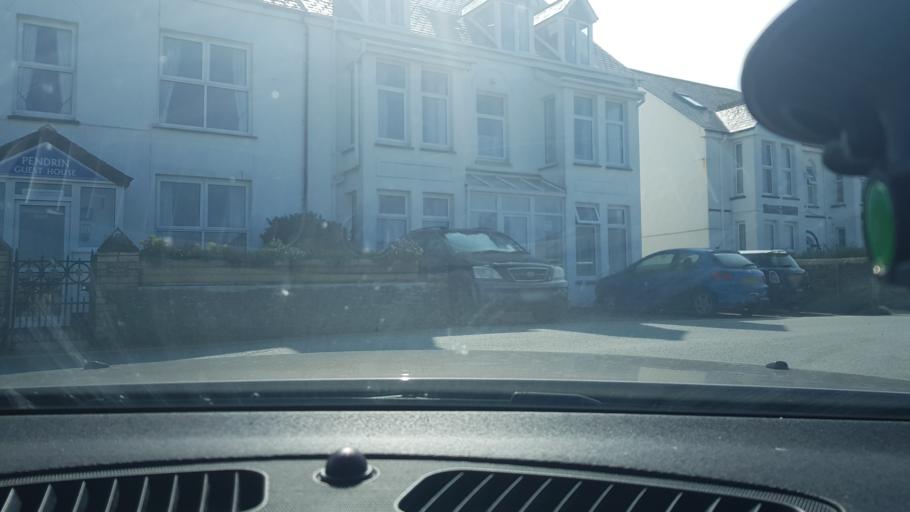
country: GB
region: England
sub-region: Cornwall
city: Tintagel
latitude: 50.6665
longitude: -4.7517
